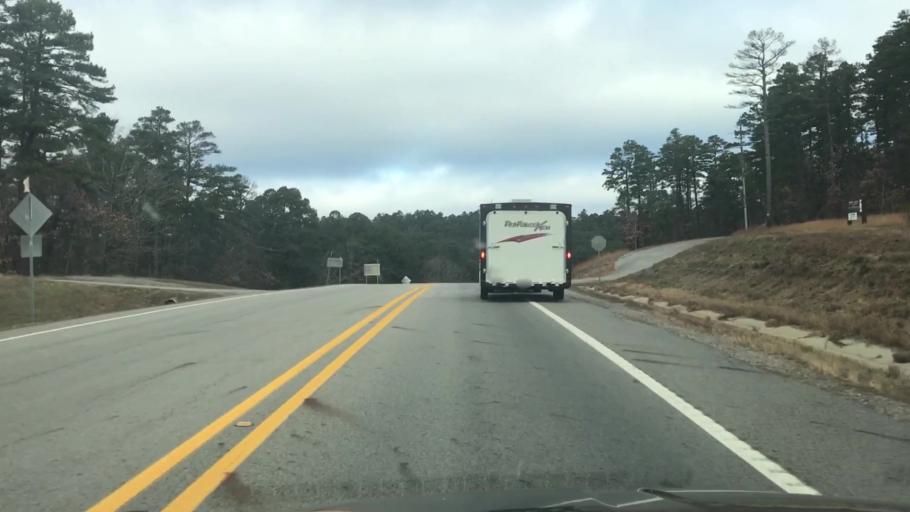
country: US
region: Arkansas
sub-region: Montgomery County
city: Mount Ida
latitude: 34.6806
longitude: -93.7881
